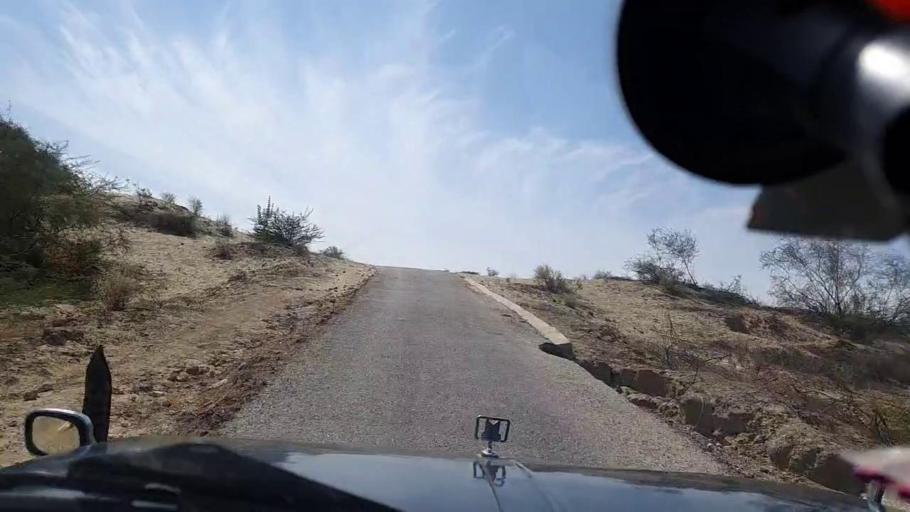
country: PK
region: Sindh
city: Diplo
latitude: 24.4004
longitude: 69.5885
